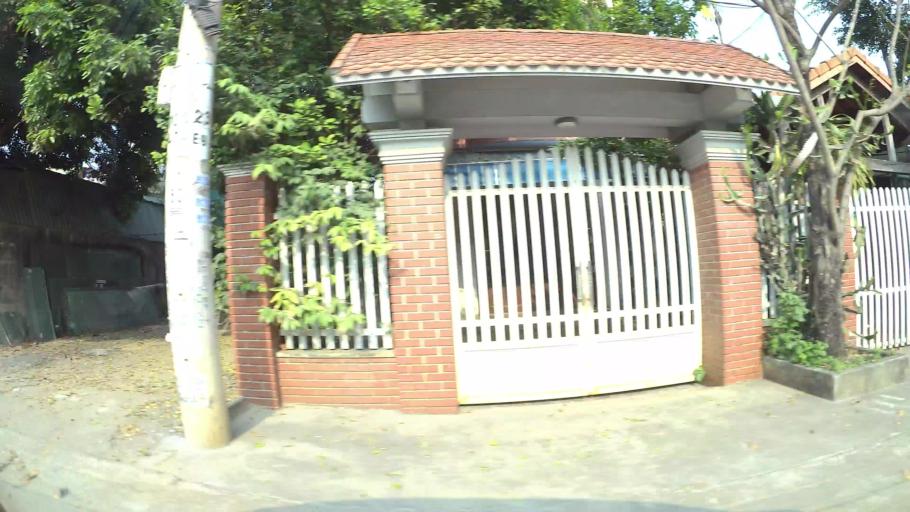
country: VN
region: Da Nang
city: Lien Chieu
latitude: 16.0552
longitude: 108.1667
